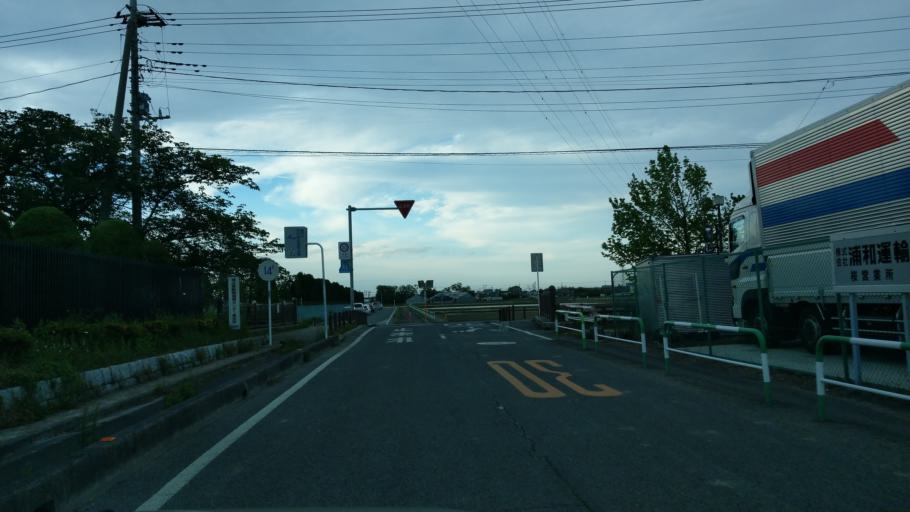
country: JP
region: Saitama
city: Yono
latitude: 35.8774
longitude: 139.5935
